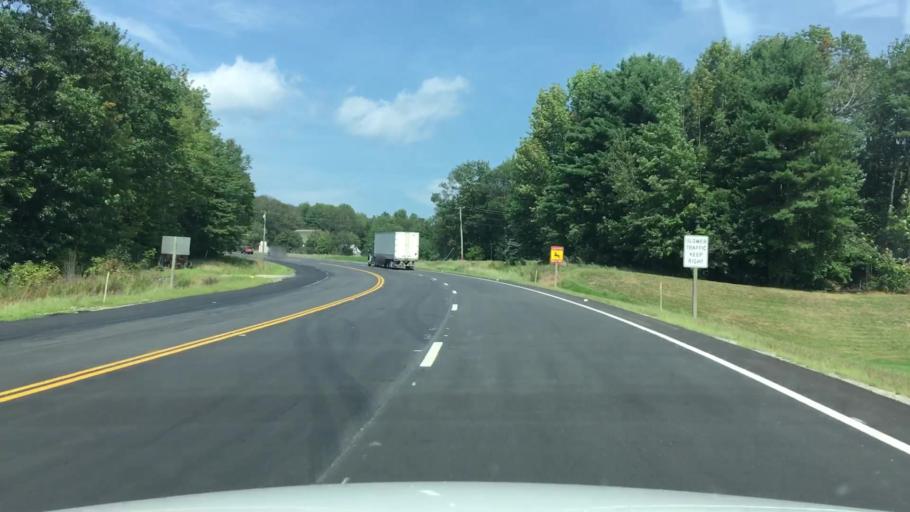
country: US
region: Maine
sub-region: Androscoggin County
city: Turner
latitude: 44.2584
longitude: -70.2589
